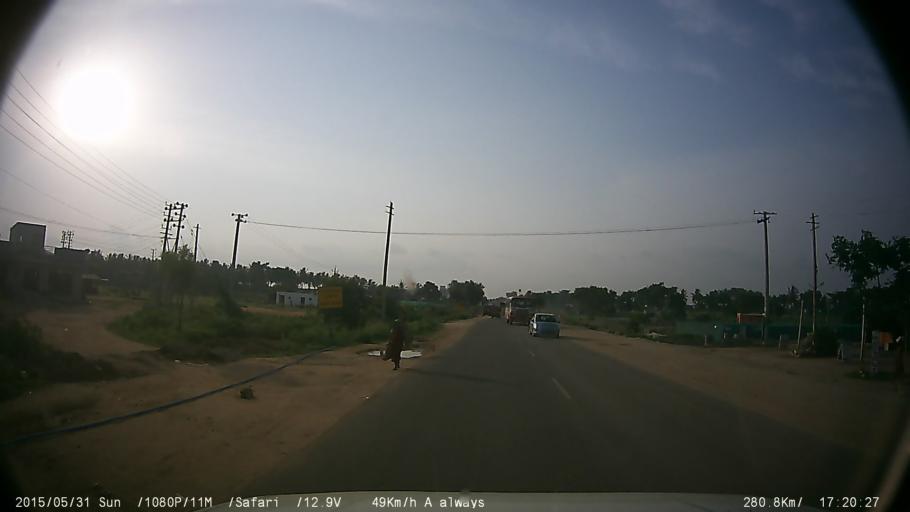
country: IN
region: Karnataka
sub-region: Chamrajnagar
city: Gundlupet
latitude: 11.8235
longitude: 76.6812
